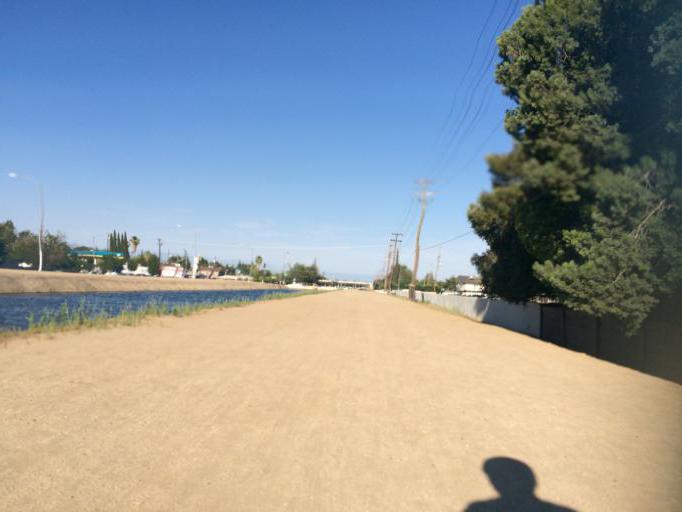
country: US
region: California
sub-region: Fresno County
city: Fresno
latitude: 36.7647
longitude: -119.7566
